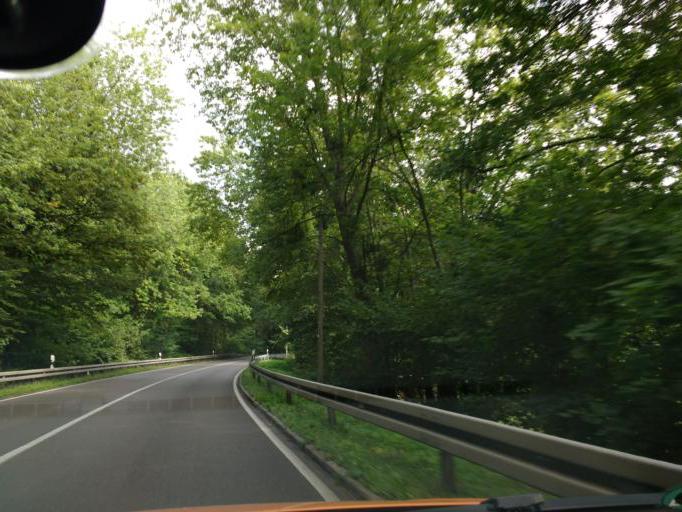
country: DE
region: Brandenburg
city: Marienwerder
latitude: 52.8569
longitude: 13.6165
